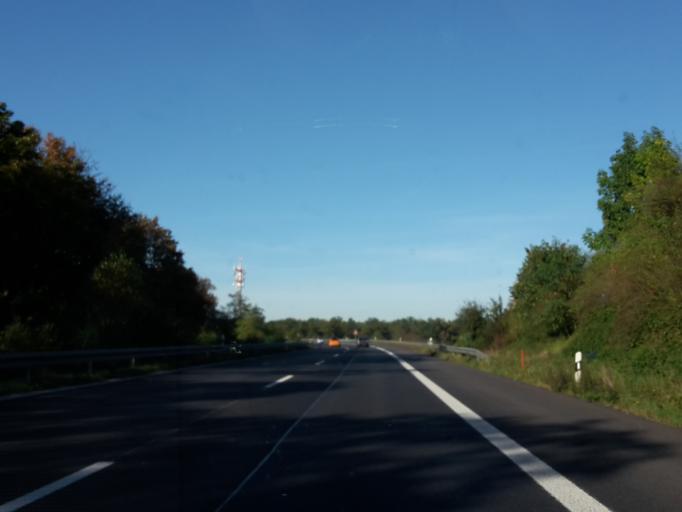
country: DE
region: Hesse
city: Viernheim
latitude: 49.5498
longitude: 8.5595
